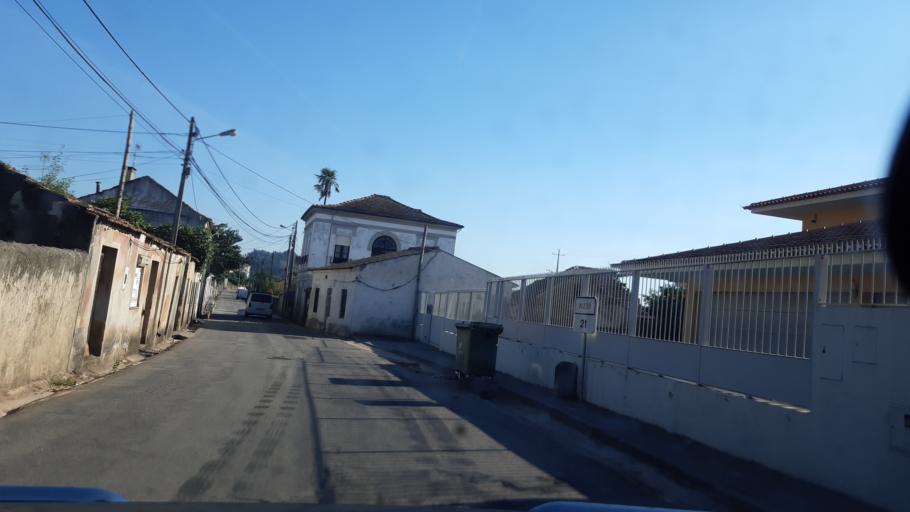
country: PT
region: Aveiro
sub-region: Agueda
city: Agueda
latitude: 40.5700
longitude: -8.4340
